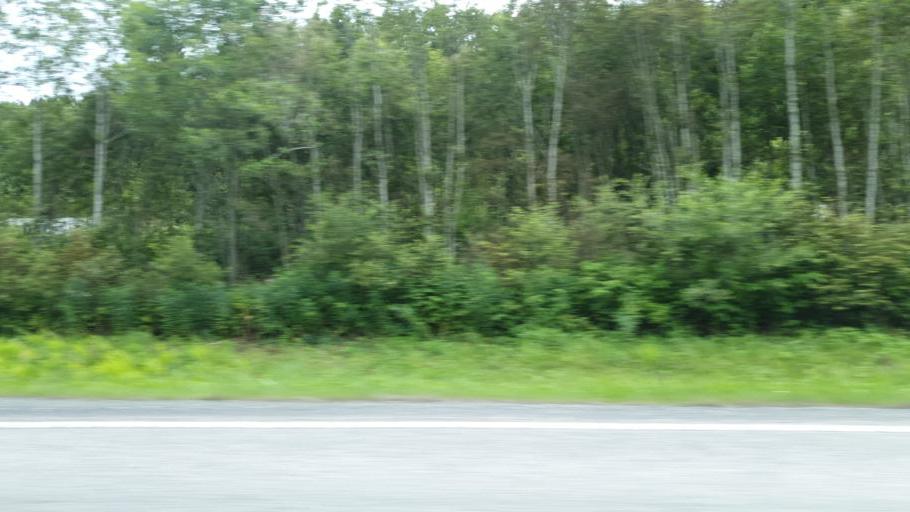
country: NO
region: Sor-Trondelag
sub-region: Midtre Gauldal
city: Storen
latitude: 62.9880
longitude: 10.2452
